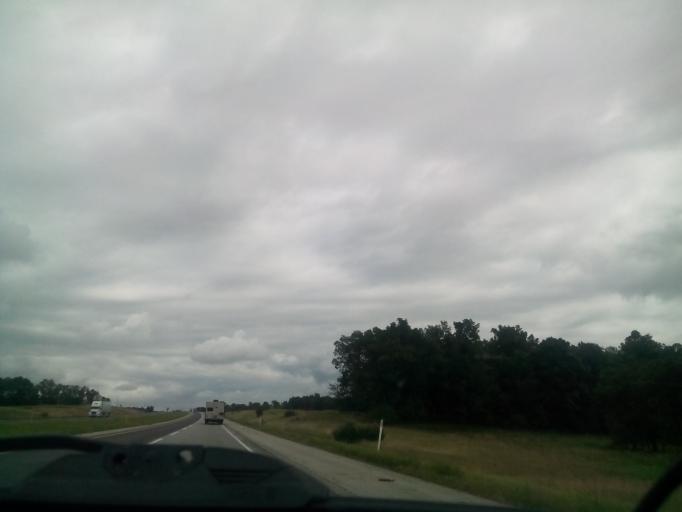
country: US
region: Michigan
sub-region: Saint Joseph County
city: Sturgis
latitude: 41.7409
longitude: -85.3043
